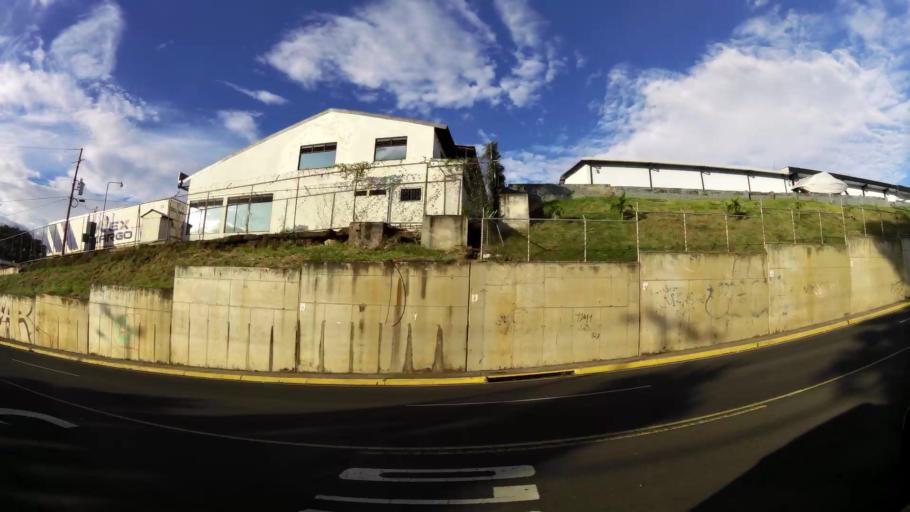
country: CR
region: Heredia
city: Llorente
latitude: 10.0032
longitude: -84.1678
